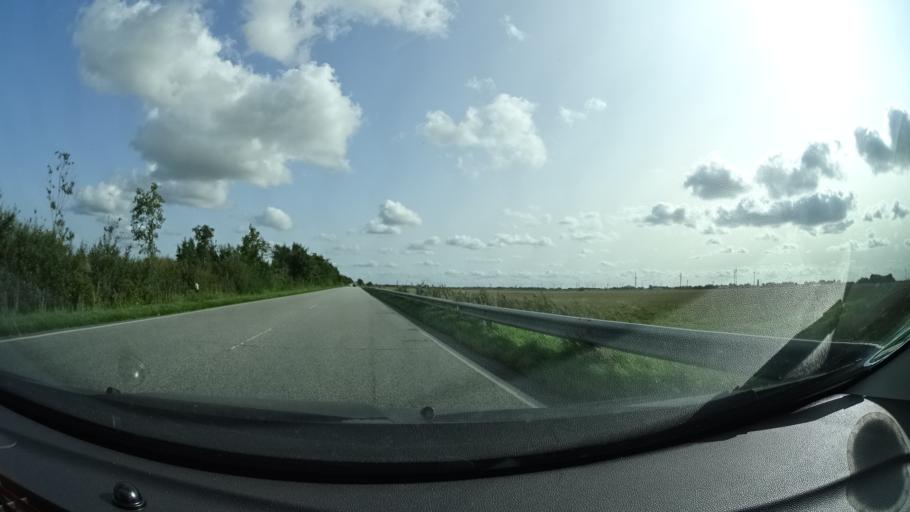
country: DE
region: Schleswig-Holstein
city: Stelle-Wittenwurth
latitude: 54.2331
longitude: 9.0376
